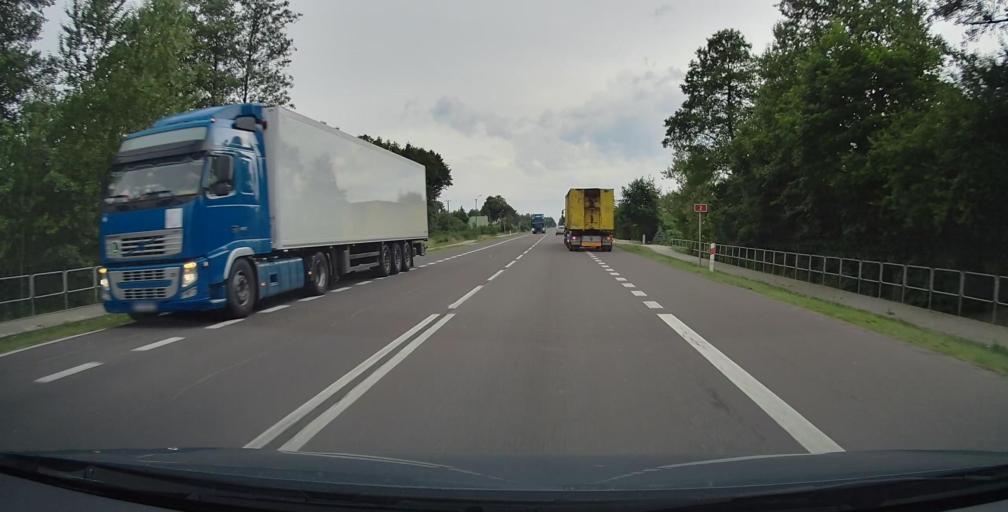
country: PL
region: Lublin Voivodeship
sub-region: Powiat bialski
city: Zalesie
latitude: 52.0371
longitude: 23.4673
